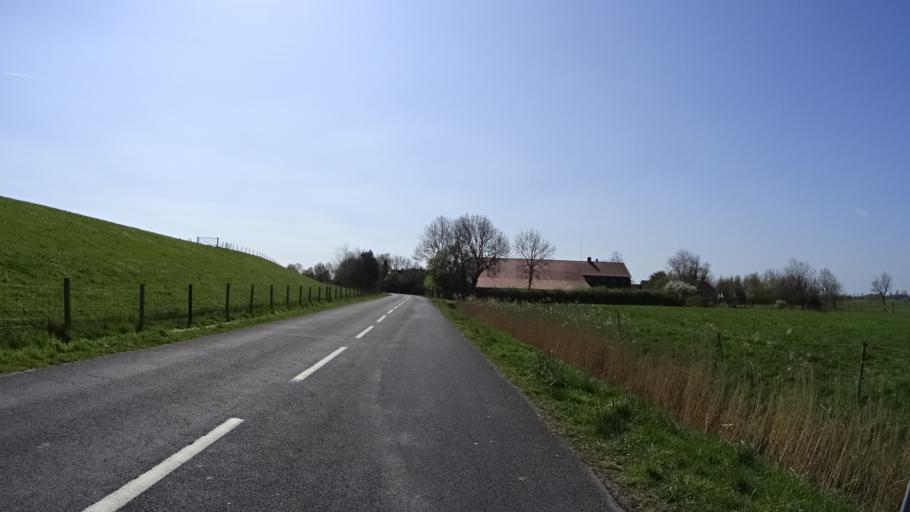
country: DE
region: Lower Saxony
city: Weener
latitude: 53.1944
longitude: 7.4009
